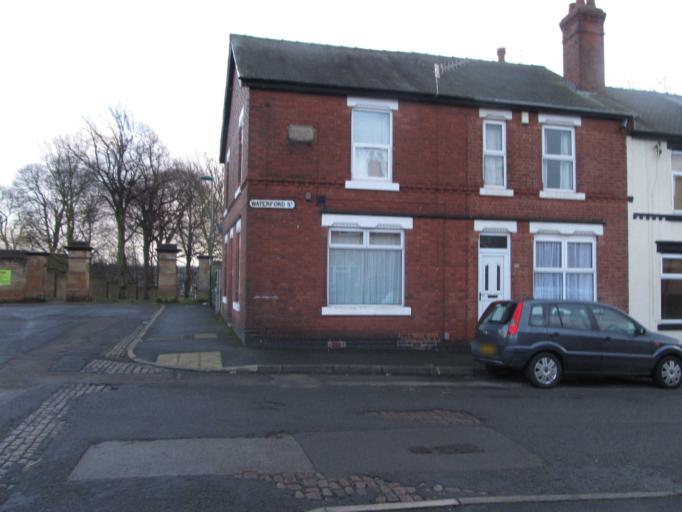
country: GB
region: England
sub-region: Nottingham
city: Nottingham
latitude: 52.9868
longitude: -1.1783
